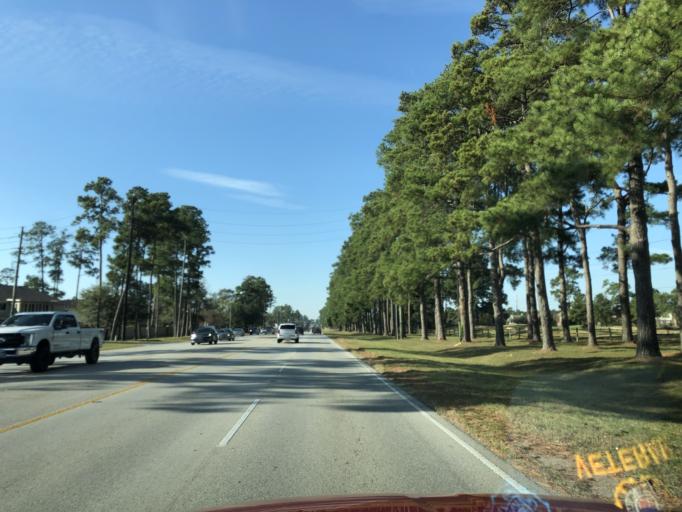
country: US
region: Texas
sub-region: Harris County
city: Tomball
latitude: 30.0296
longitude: -95.5588
